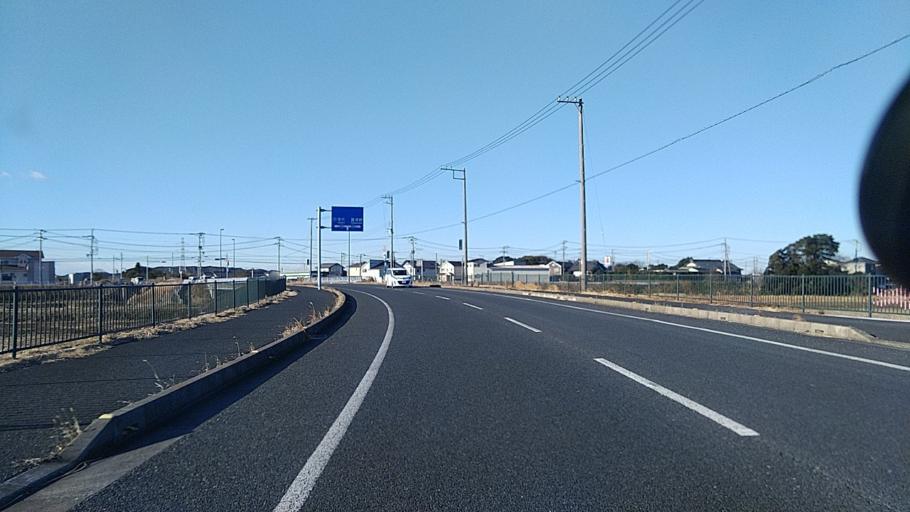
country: JP
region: Chiba
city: Kimitsu
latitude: 35.3218
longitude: 139.8848
